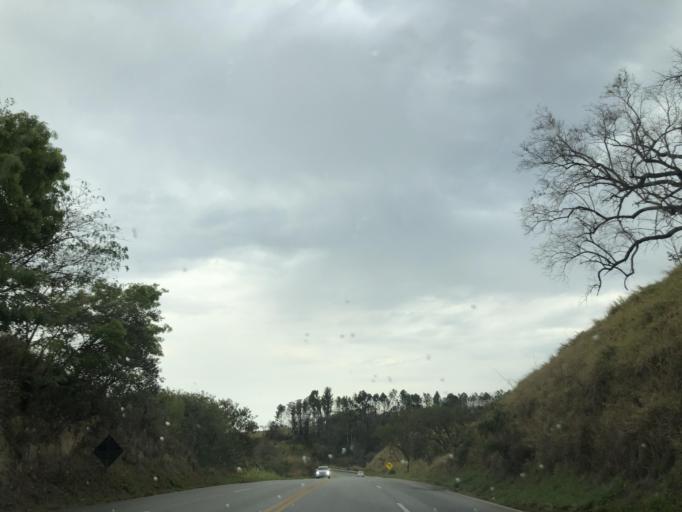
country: BR
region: Sao Paulo
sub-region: Salto De Pirapora
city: Salto de Pirapora
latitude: -23.6939
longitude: -47.6095
